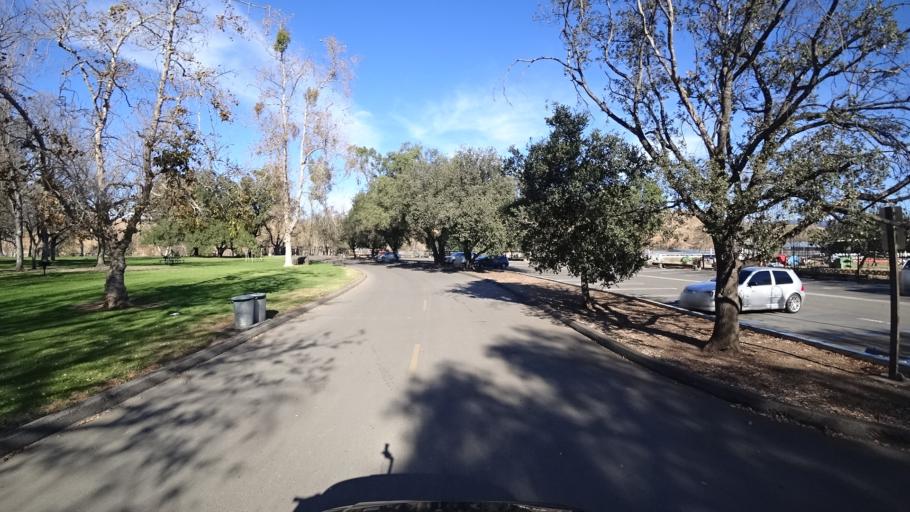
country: US
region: California
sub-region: Orange County
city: North Tustin
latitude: 33.7980
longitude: -117.7529
